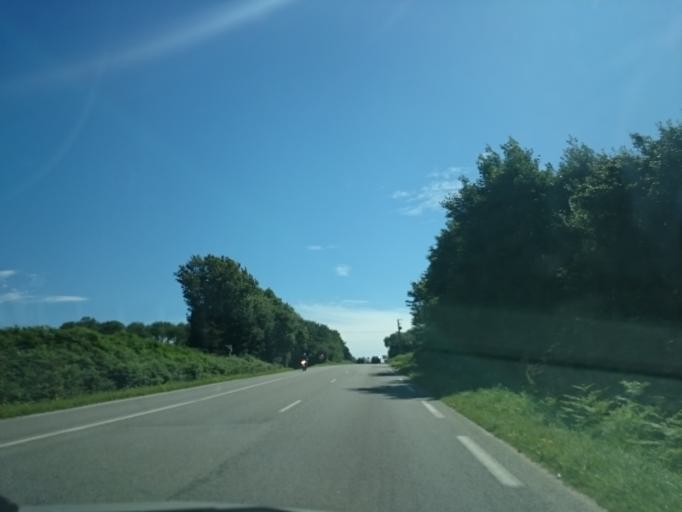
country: FR
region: Brittany
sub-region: Departement du Finistere
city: Guilers
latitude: 48.4277
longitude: -4.5836
